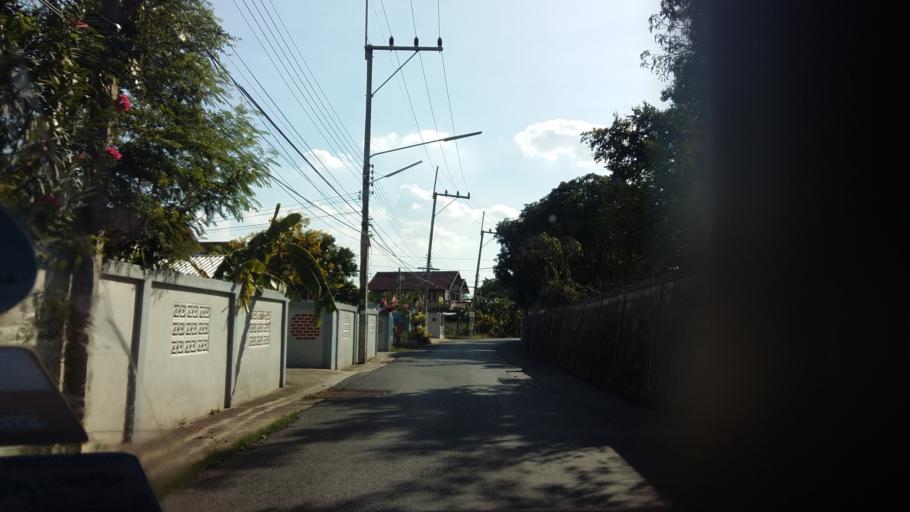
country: TH
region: Lop Buri
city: Lop Buri
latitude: 14.8310
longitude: 100.6478
